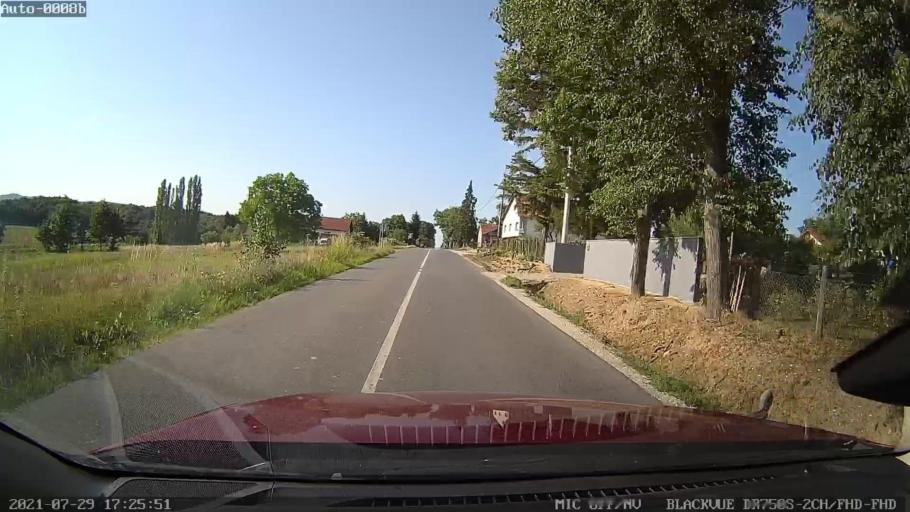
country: HR
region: Varazdinska
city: Ivanec
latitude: 46.2497
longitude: 16.1182
